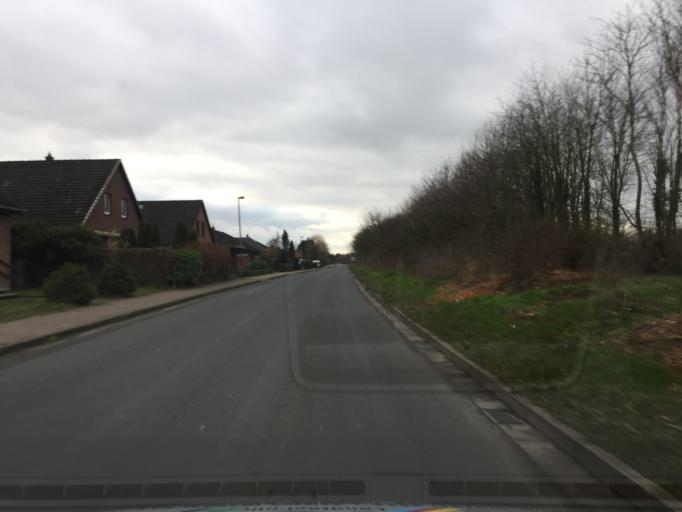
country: DE
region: Lower Saxony
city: Stolzenau
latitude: 52.5229
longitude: 9.0718
